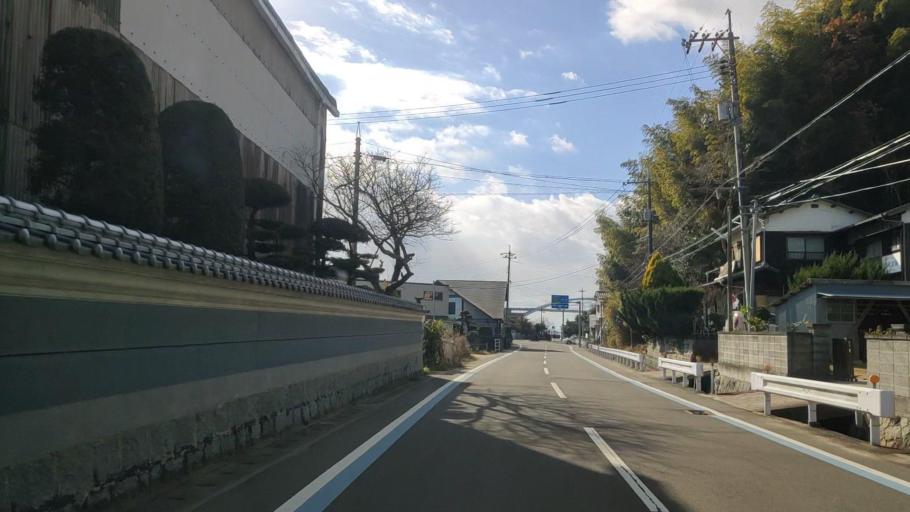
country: JP
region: Hiroshima
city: Innoshima
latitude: 34.2219
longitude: 133.0683
